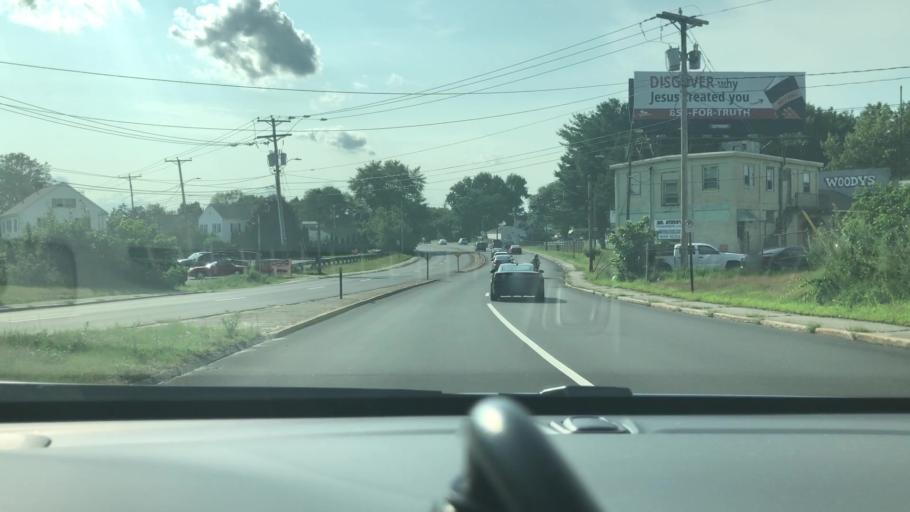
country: US
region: New Hampshire
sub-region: Hillsborough County
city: Manchester
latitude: 42.9731
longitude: -71.4583
